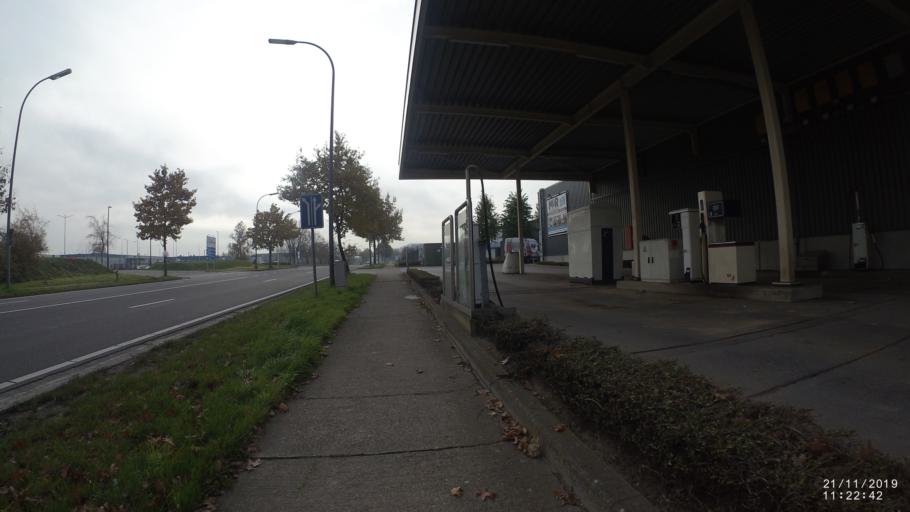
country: BE
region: Flanders
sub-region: Provincie Limburg
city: Sint-Truiden
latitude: 50.8177
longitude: 5.2070
